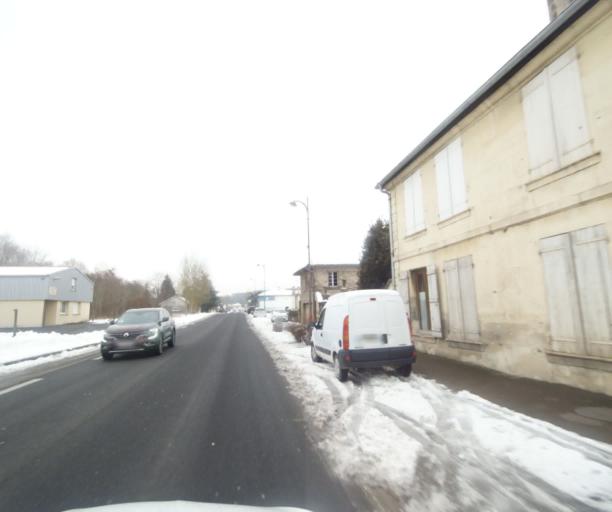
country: FR
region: Champagne-Ardenne
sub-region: Departement de la Haute-Marne
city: Villiers-en-Lieu
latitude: 48.6184
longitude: 4.9011
